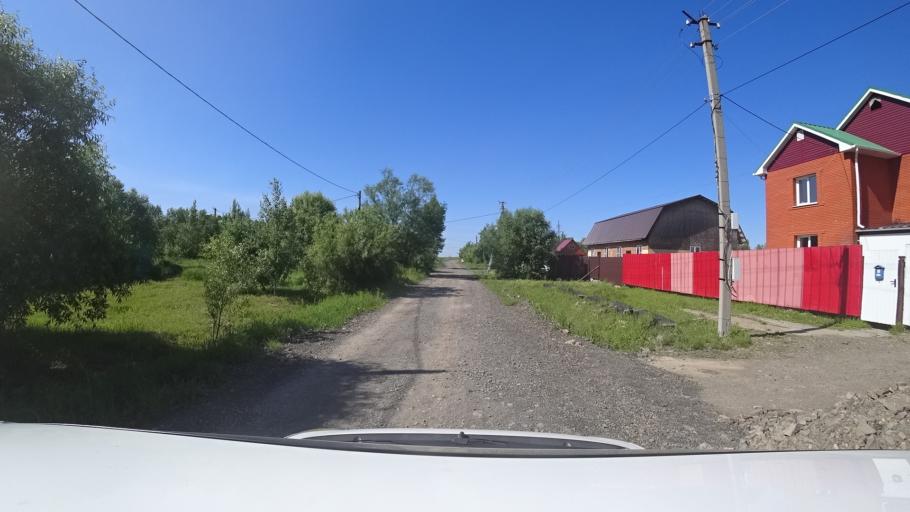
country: RU
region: Khabarovsk Krai
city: Topolevo
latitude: 48.5519
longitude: 135.1691
